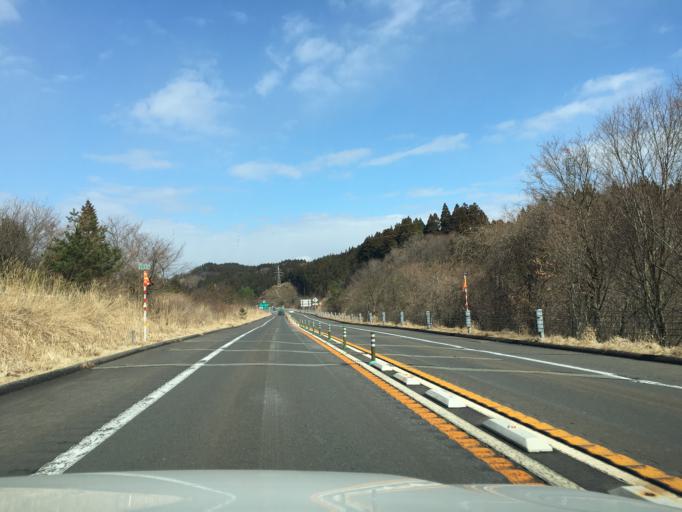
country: JP
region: Akita
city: Akita
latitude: 39.7706
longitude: 140.1210
